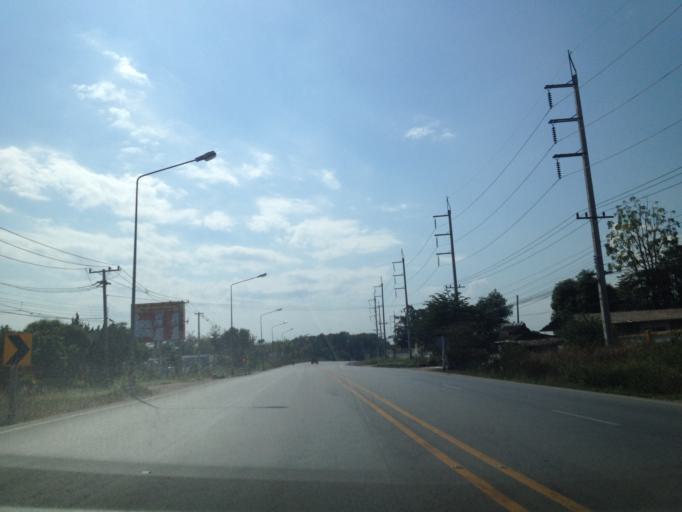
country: TH
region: Chiang Mai
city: Chom Thong
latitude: 18.3461
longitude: 98.6803
